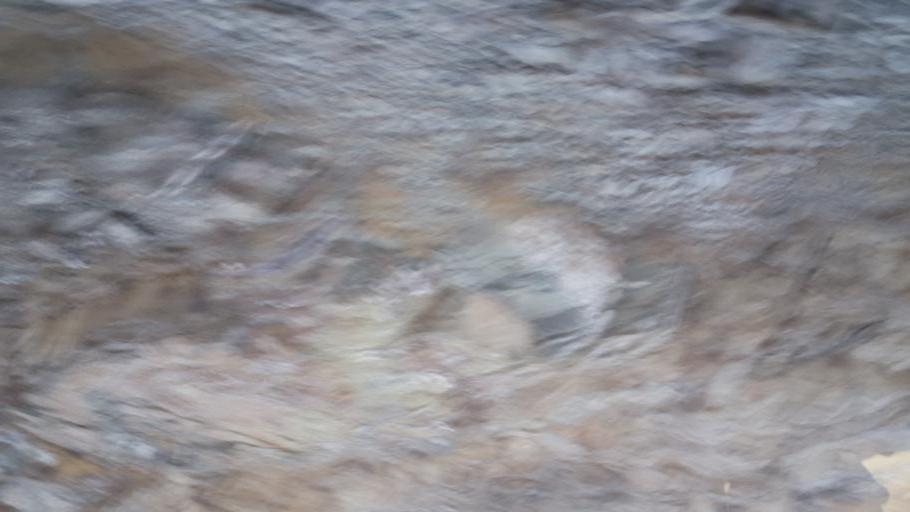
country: TR
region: Eskisehir
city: Kirka
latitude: 39.3320
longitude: 30.5775
